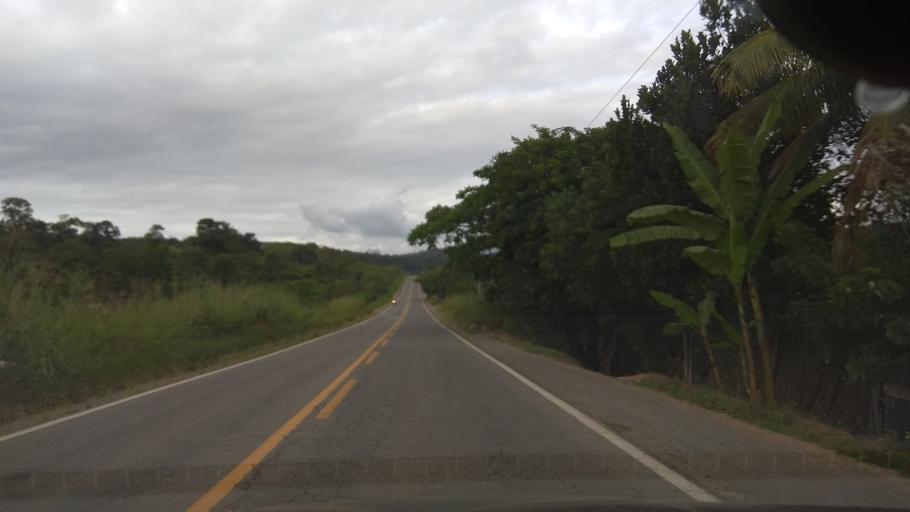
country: BR
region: Bahia
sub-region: Ipiau
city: Ipiau
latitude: -14.1433
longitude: -39.7186
